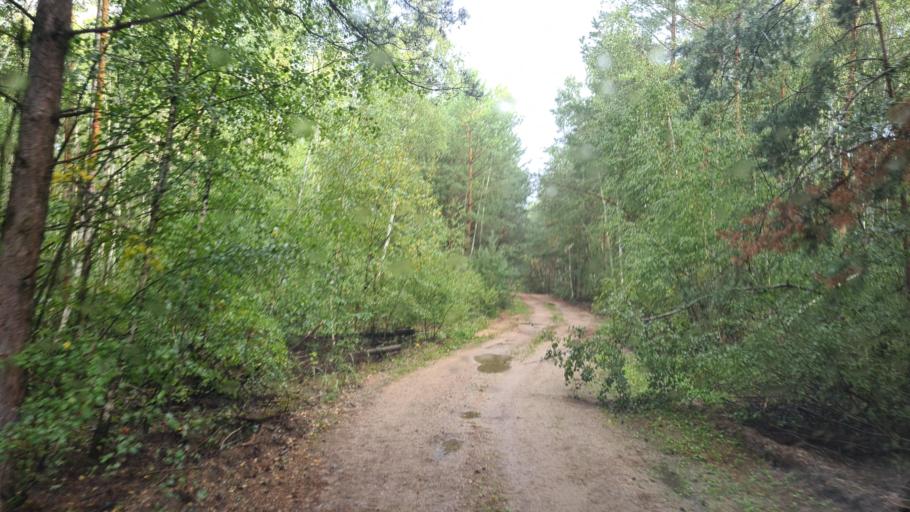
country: DE
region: Brandenburg
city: Sallgast
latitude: 51.5859
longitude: 13.8016
